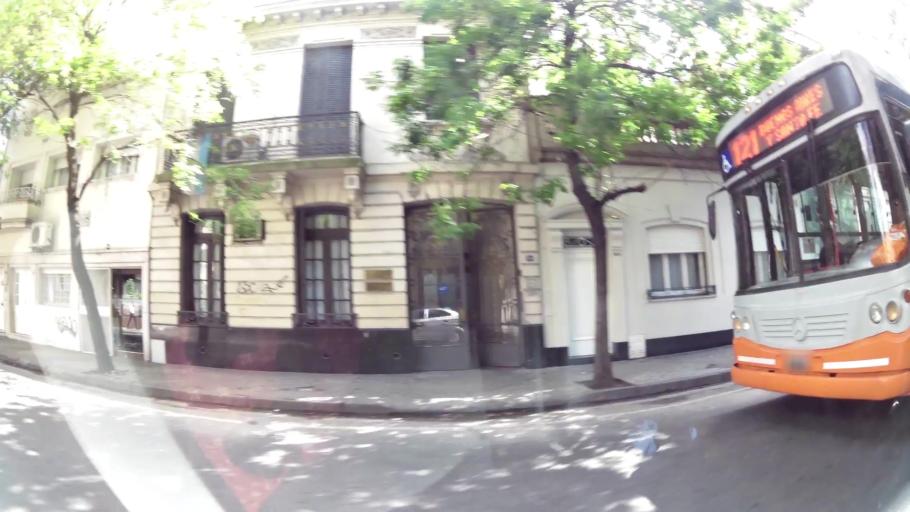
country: AR
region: Santa Fe
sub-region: Departamento de Rosario
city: Rosario
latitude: -32.9433
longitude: -60.6479
